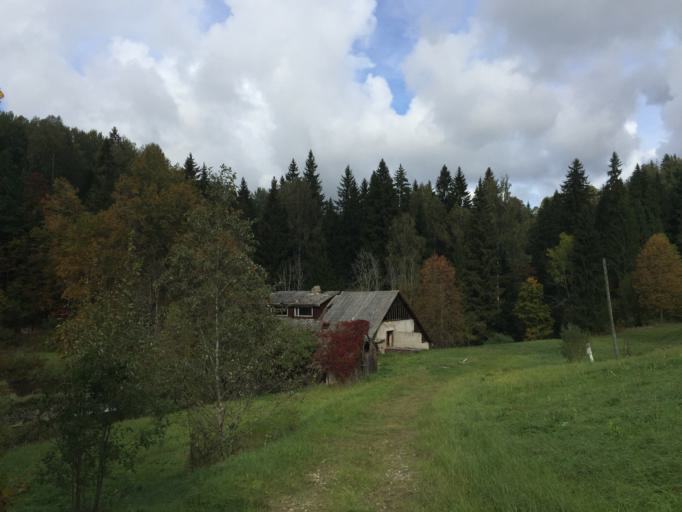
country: LV
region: Ligatne
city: Ligatne
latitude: 57.2140
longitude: 25.0636
